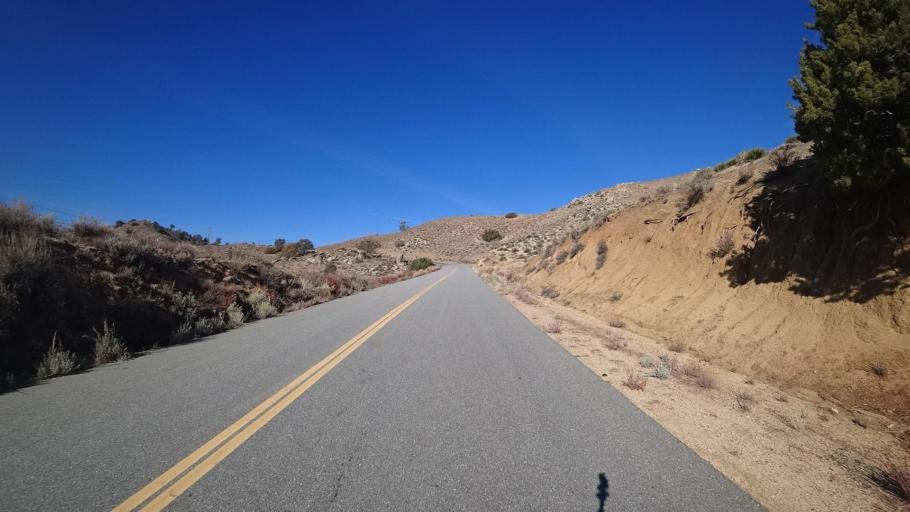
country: US
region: California
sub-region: Kern County
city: Bodfish
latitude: 35.3818
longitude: -118.4078
